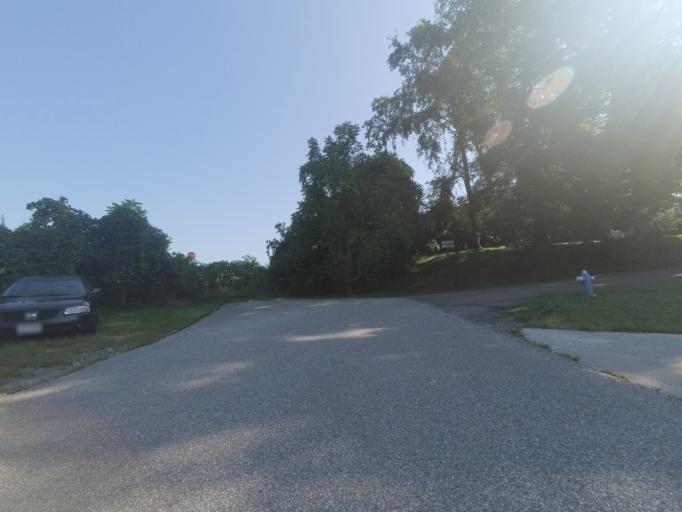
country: US
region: West Virginia
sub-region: Cabell County
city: Huntington
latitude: 38.4327
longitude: -82.4572
